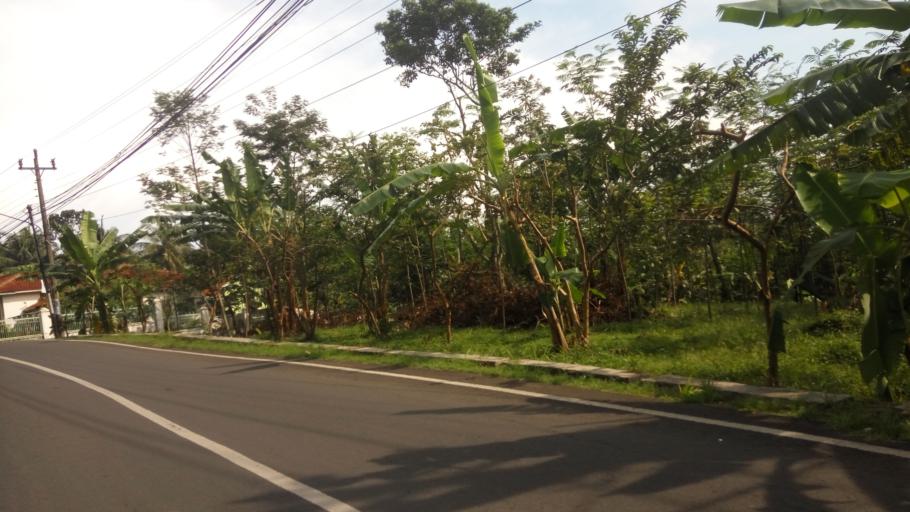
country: ID
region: Central Java
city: Ungaran
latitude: -7.1436
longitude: 110.4163
